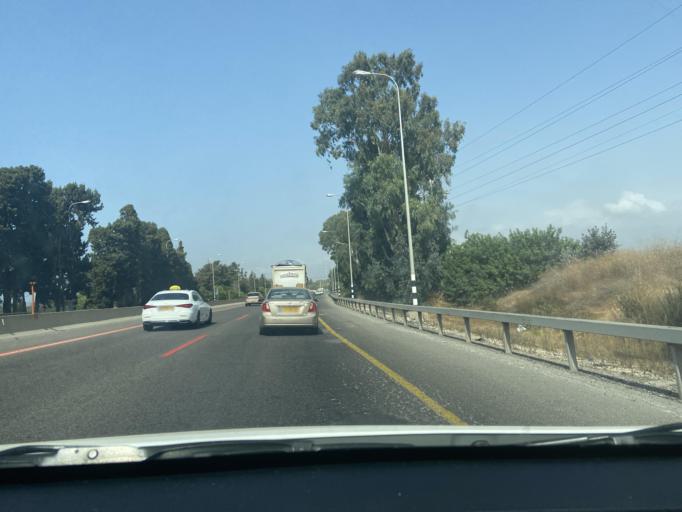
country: IL
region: Northern District
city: El Mazra`a
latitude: 32.9545
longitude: 35.0911
